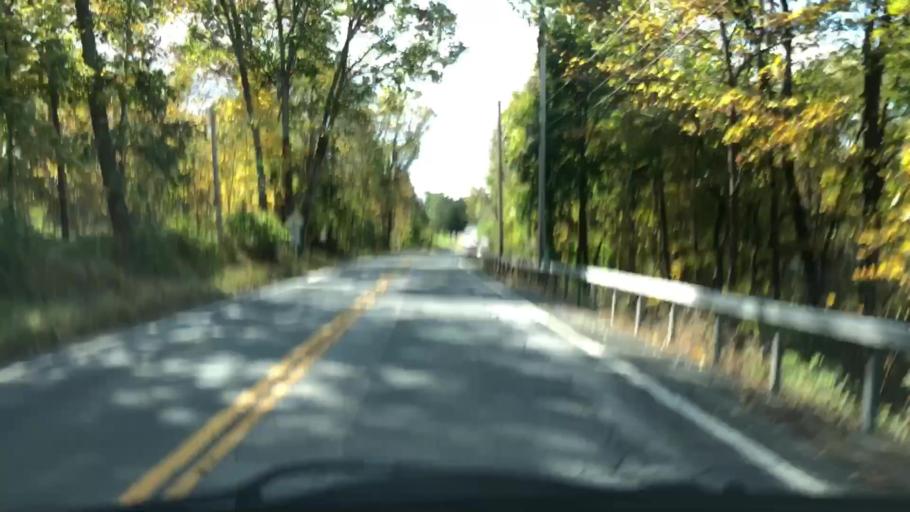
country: US
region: New York
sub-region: Orange County
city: Walden
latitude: 41.5802
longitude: -74.1883
